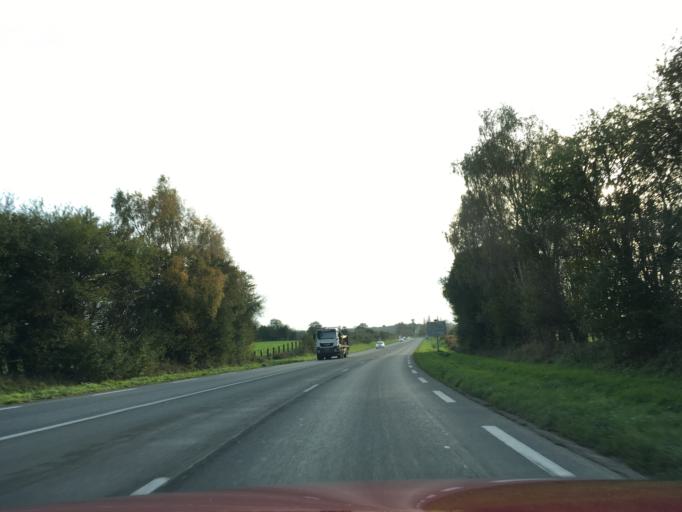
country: FR
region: Lower Normandy
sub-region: Departement de la Manche
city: Saint-Planchers
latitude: 48.8321
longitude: -1.5388
